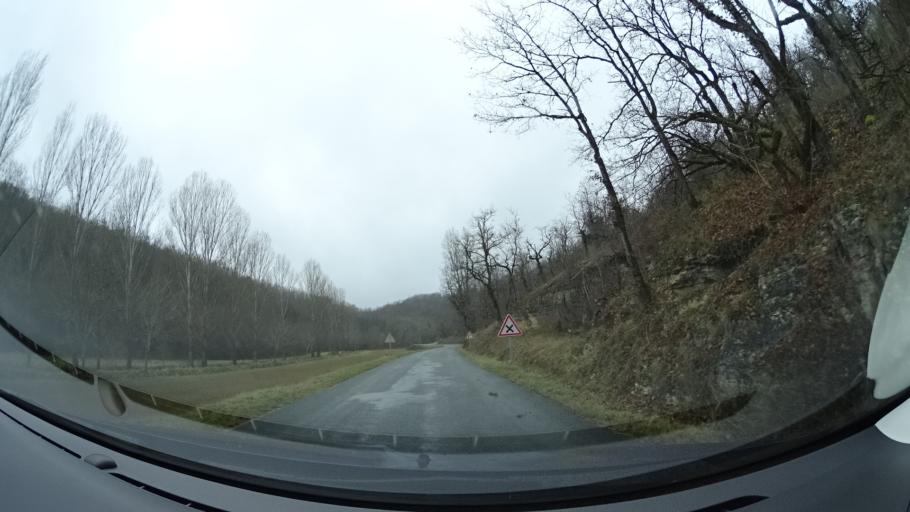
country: FR
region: Midi-Pyrenees
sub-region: Departement du Lot
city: Prayssac
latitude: 44.4355
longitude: 1.2084
